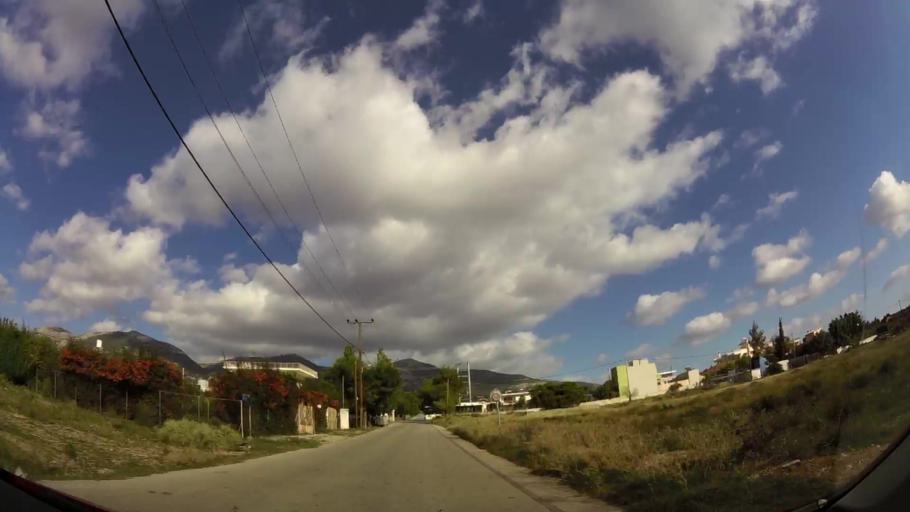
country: GR
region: Attica
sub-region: Nomarchia Anatolikis Attikis
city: Thrakomakedones
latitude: 38.1142
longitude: 23.7567
